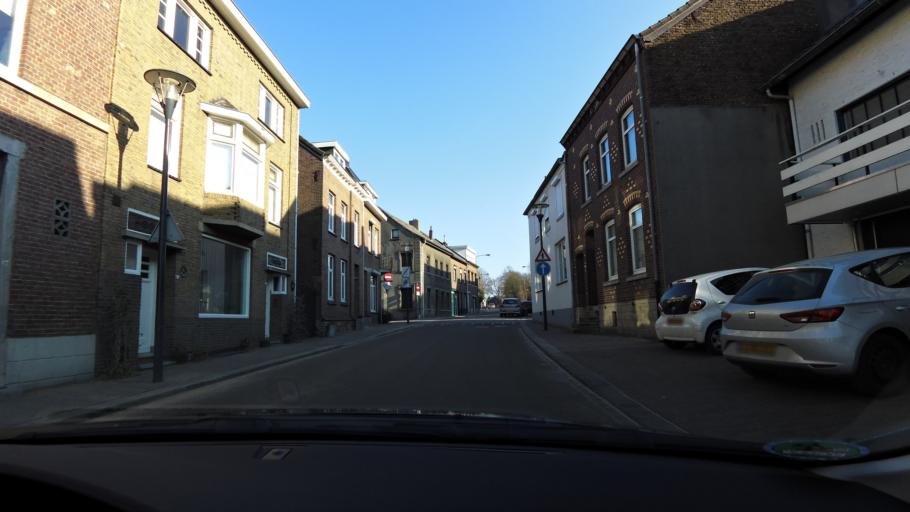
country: NL
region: Limburg
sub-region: Gemeente Meerssen
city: Meerssen
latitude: 50.8853
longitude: 5.7567
